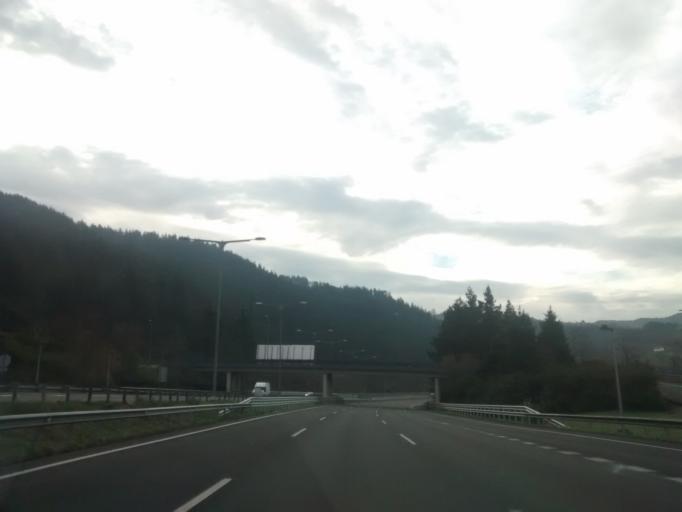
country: ES
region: Basque Country
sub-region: Bizkaia
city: Arrigorriaga
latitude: 43.1901
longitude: -2.8956
